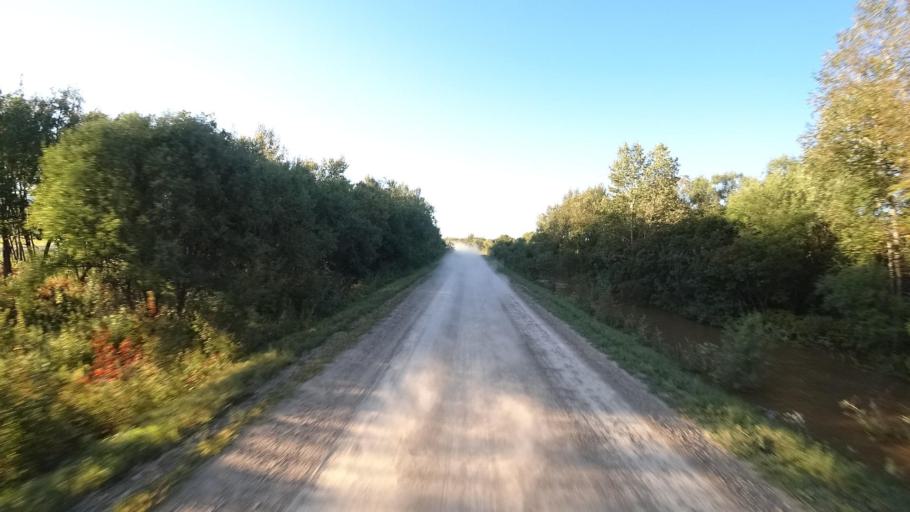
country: RU
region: Primorskiy
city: Kirovskiy
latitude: 44.7814
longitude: 133.6258
